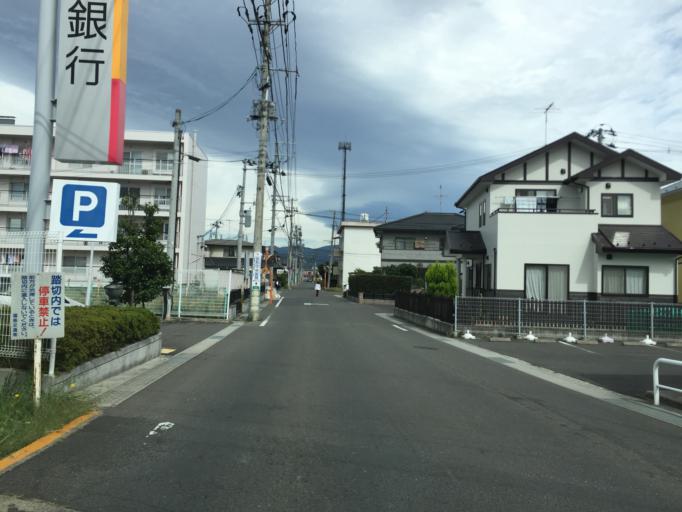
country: JP
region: Fukushima
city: Fukushima-shi
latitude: 37.7730
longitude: 140.4505
